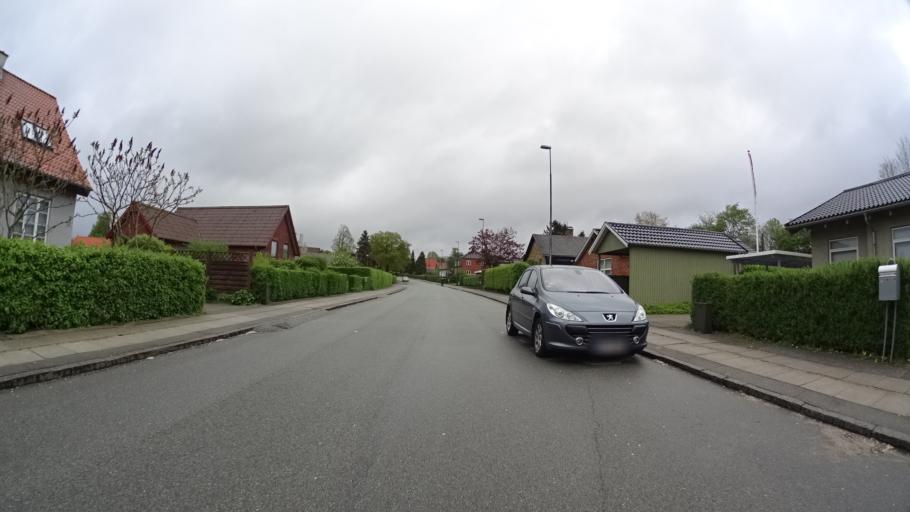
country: DK
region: Central Jutland
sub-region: Arhus Kommune
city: Arhus
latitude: 56.1317
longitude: 10.1728
